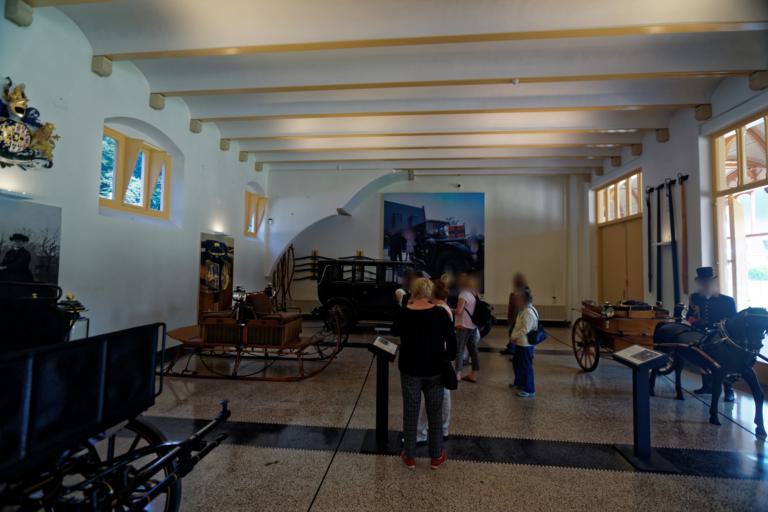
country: NL
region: Gelderland
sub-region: Gemeente Apeldoorn
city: Apeldoorn
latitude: 52.2304
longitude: 5.9415
